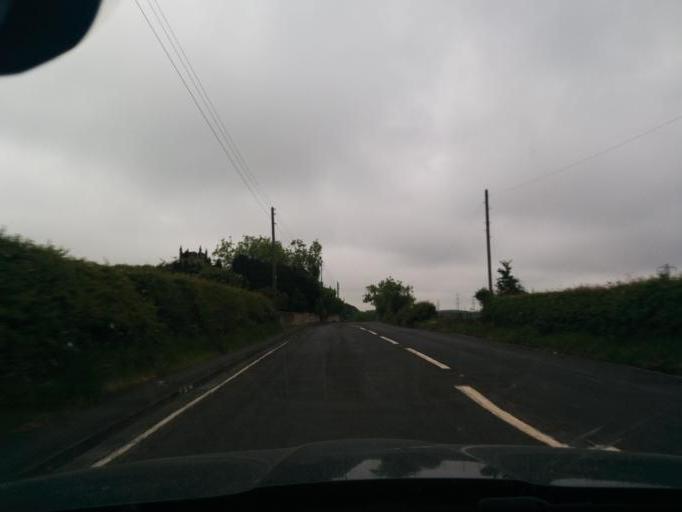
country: GB
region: England
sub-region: Northumberland
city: Bedlington
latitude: 55.1115
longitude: -1.5716
